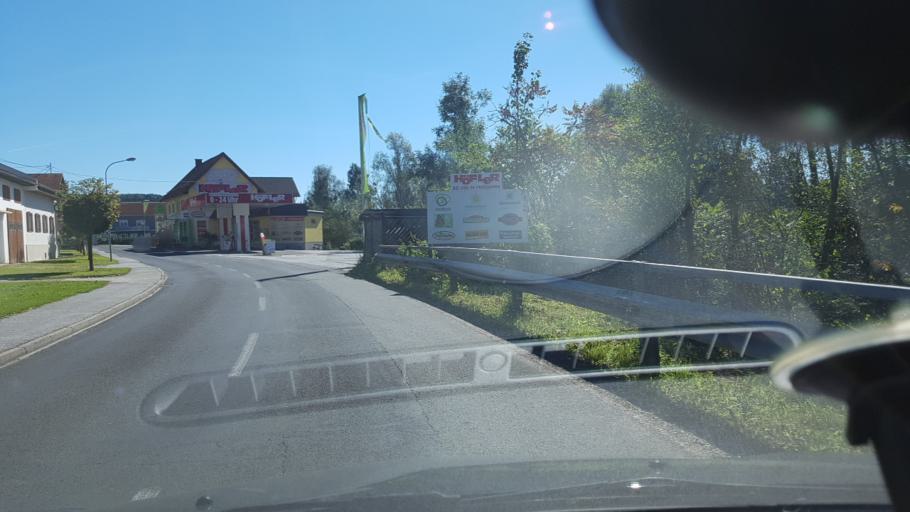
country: AT
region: Styria
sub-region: Politischer Bezirk Weiz
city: Sinabelkirchen
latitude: 47.1216
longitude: 15.8123
